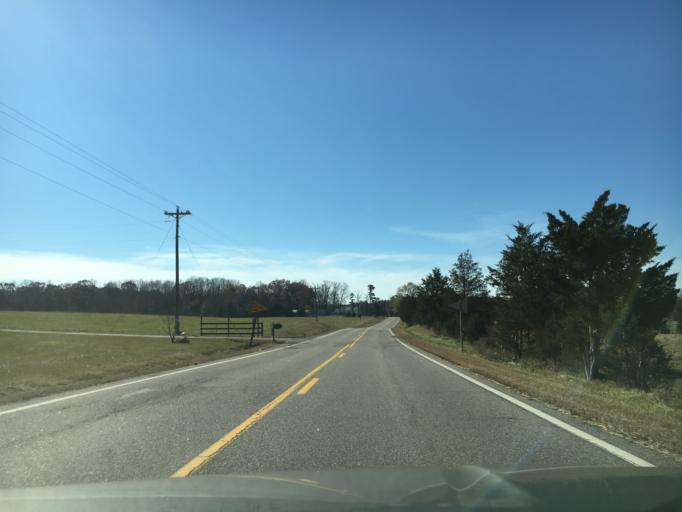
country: US
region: Virginia
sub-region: Cumberland County
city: Cumberland
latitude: 37.5342
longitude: -78.1959
